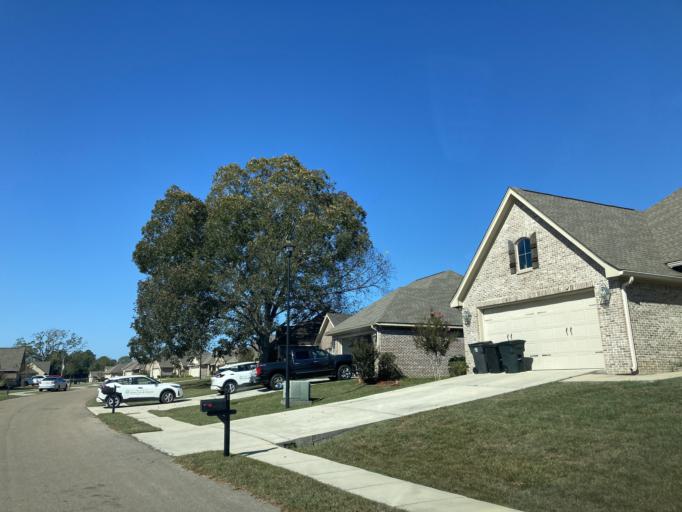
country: US
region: Mississippi
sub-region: Lamar County
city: West Hattiesburg
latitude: 31.2804
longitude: -89.4111
